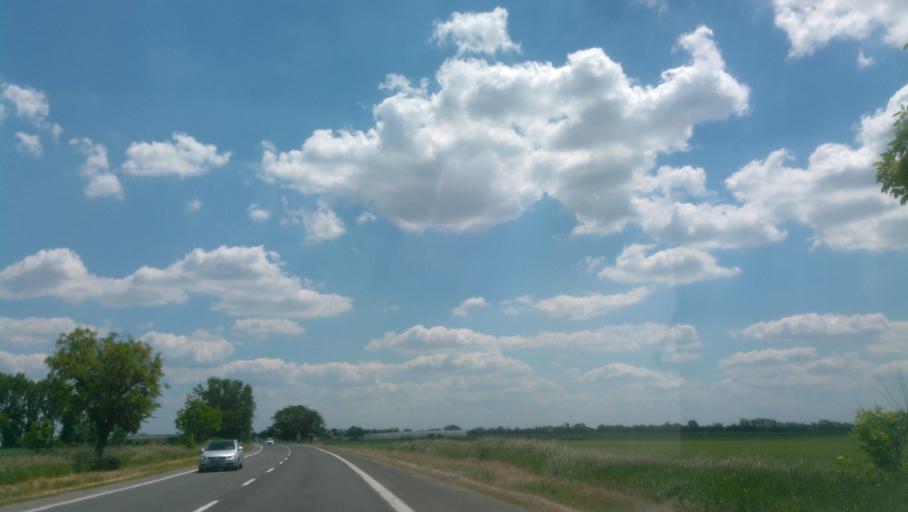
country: SK
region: Bratislavsky
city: Dunajska Luzna
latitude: 48.0583
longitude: 17.2840
